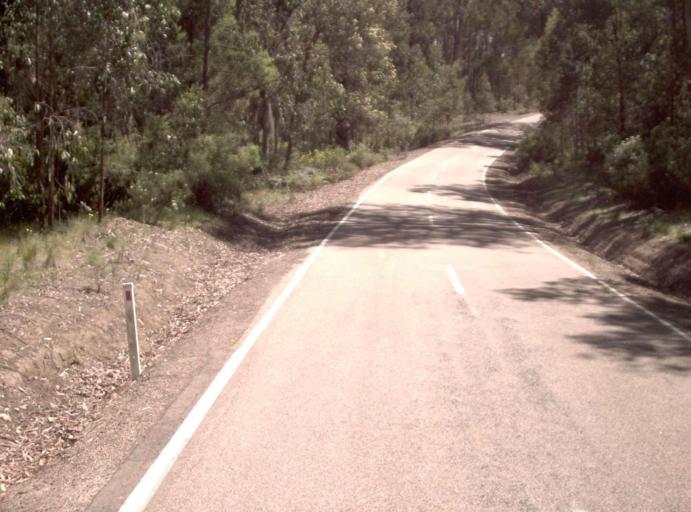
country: AU
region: Victoria
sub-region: East Gippsland
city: Lakes Entrance
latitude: -37.3013
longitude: 148.2462
